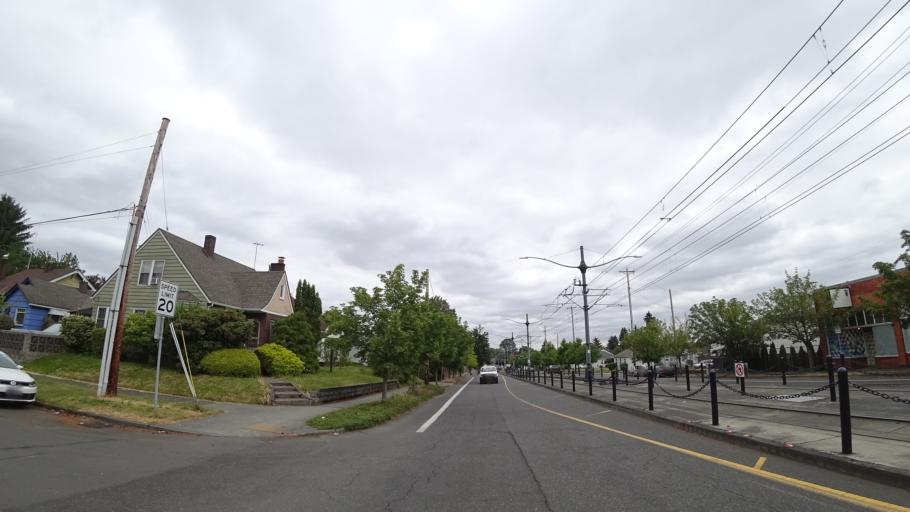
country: US
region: Oregon
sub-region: Multnomah County
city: Portland
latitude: 45.5781
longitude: -122.6822
